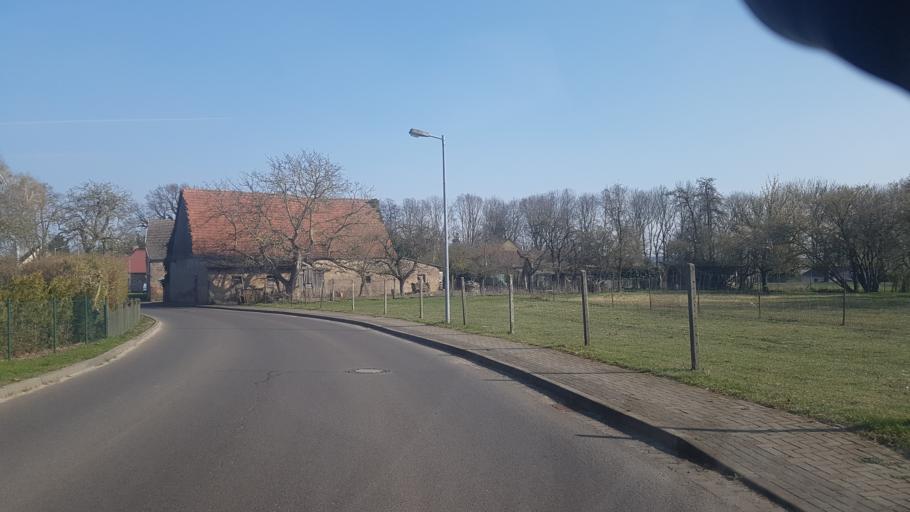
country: DE
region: Brandenburg
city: Gerswalde
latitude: 53.2174
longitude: 13.8381
